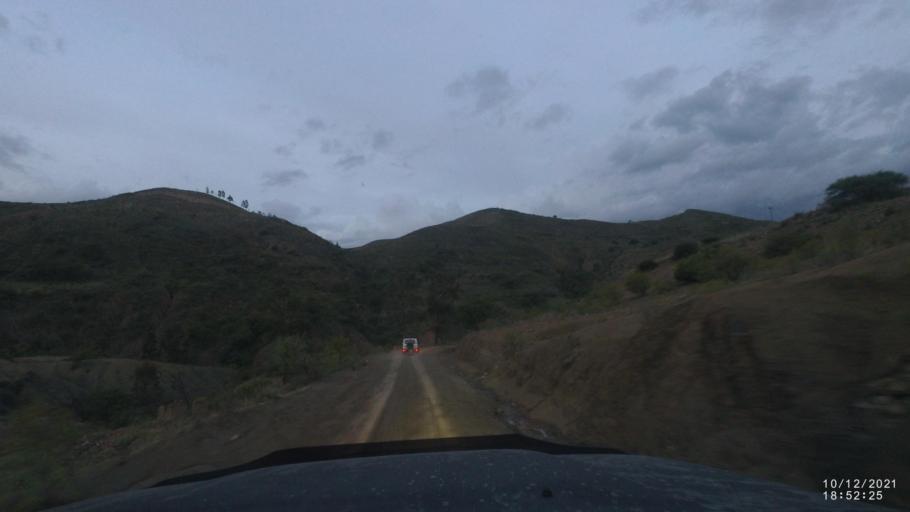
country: BO
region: Cochabamba
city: Tarata
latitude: -17.8828
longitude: -65.9631
